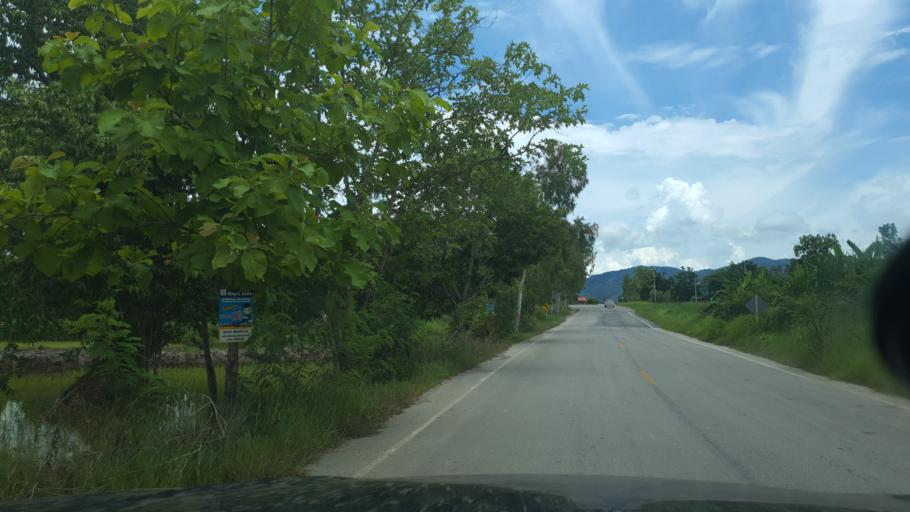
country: TH
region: Lampang
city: Sop Prap
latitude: 17.9149
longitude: 99.3885
